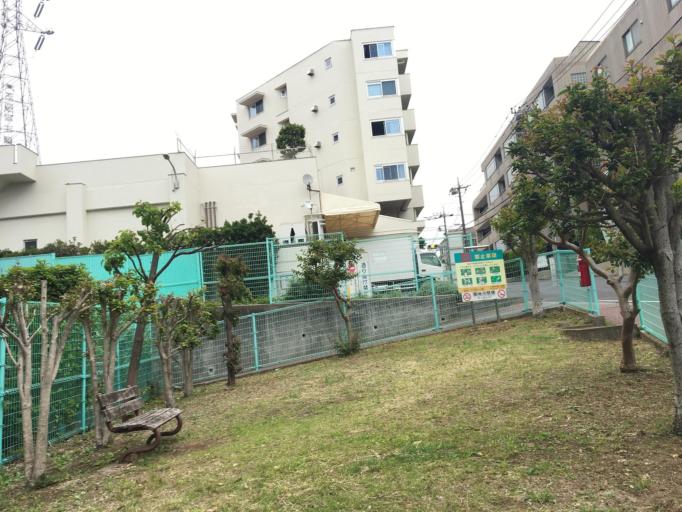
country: JP
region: Tokyo
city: Chofugaoka
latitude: 35.6608
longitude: 139.5672
